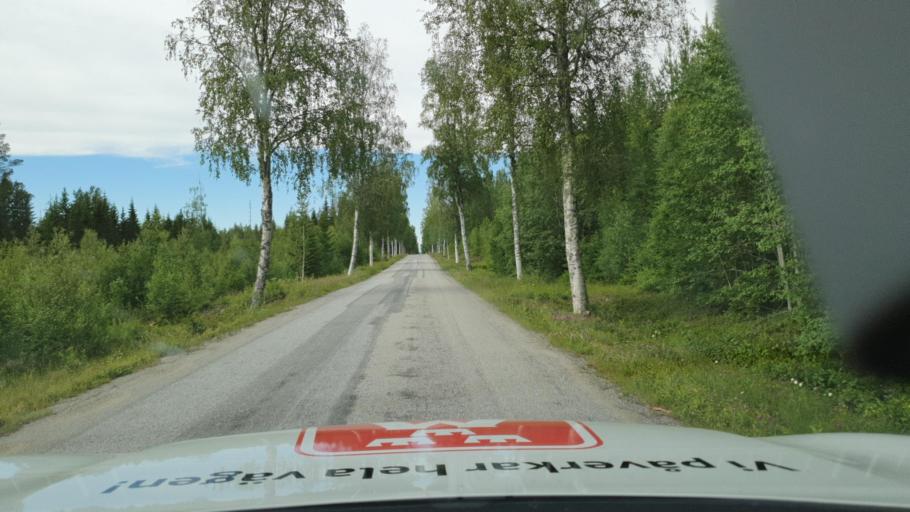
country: SE
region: Vaesterbotten
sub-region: Skelleftea Kommun
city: Burtraesk
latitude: 64.4368
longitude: 20.5035
